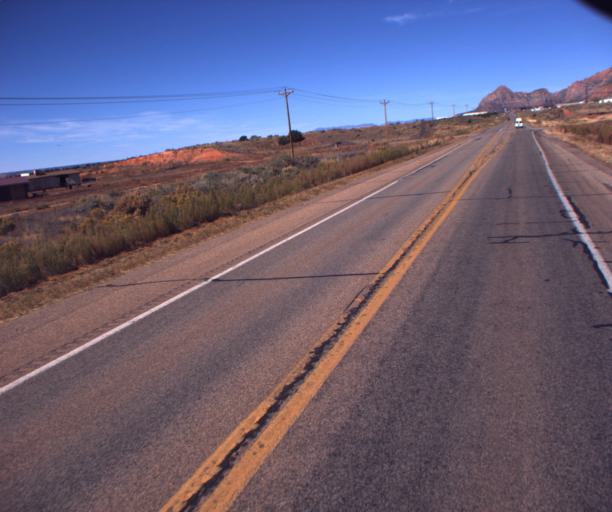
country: US
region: Arizona
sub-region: Mohave County
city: Colorado City
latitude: 36.9893
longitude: -112.9901
